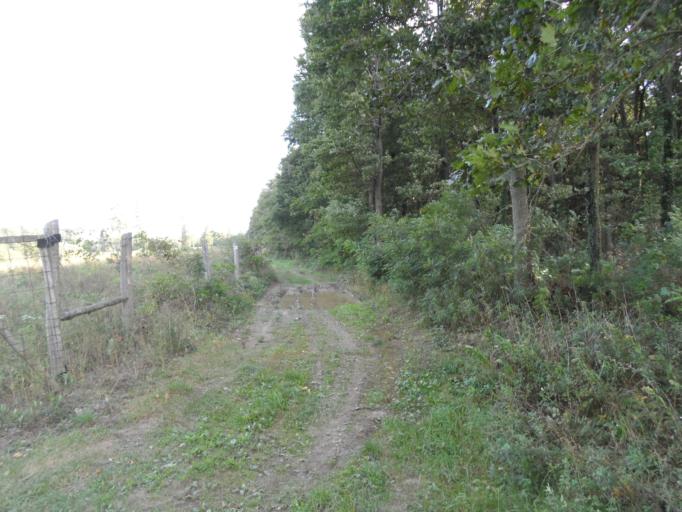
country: HU
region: Veszprem
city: Devecser
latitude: 47.1980
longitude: 17.4176
